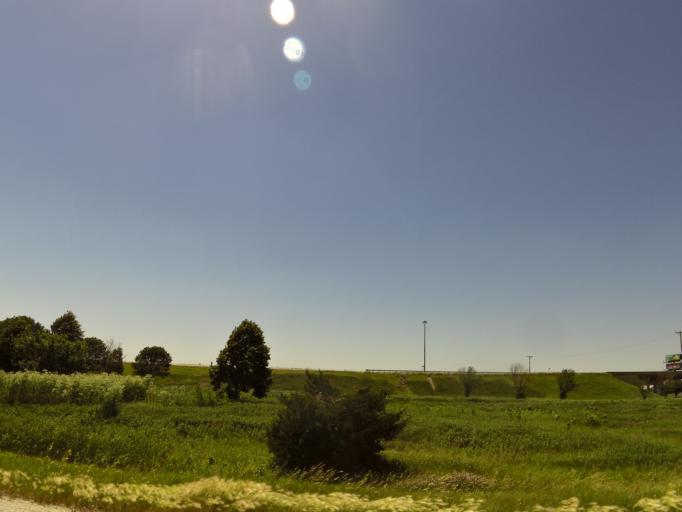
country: US
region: Illinois
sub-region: Woodford County
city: El Paso
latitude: 40.7358
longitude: -89.0322
